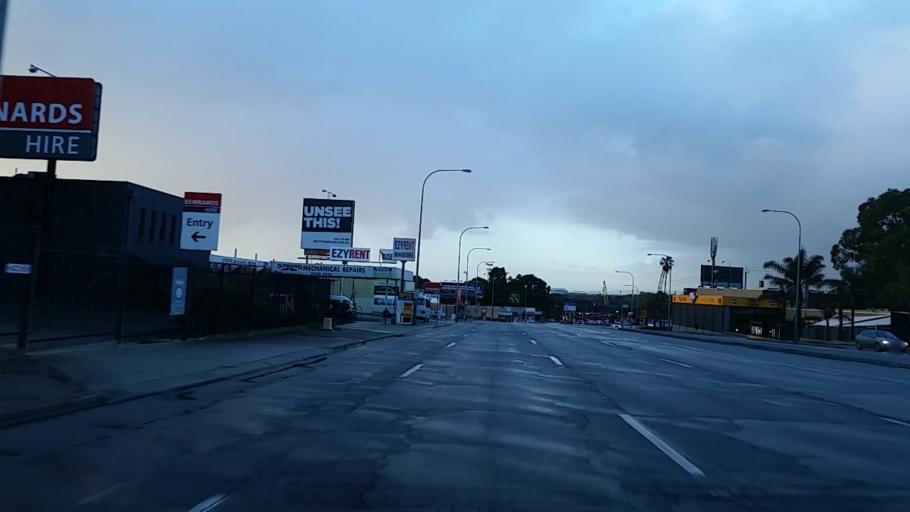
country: AU
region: South Australia
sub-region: Onkaparinga
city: Bedford Park
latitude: -35.0281
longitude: 138.5575
